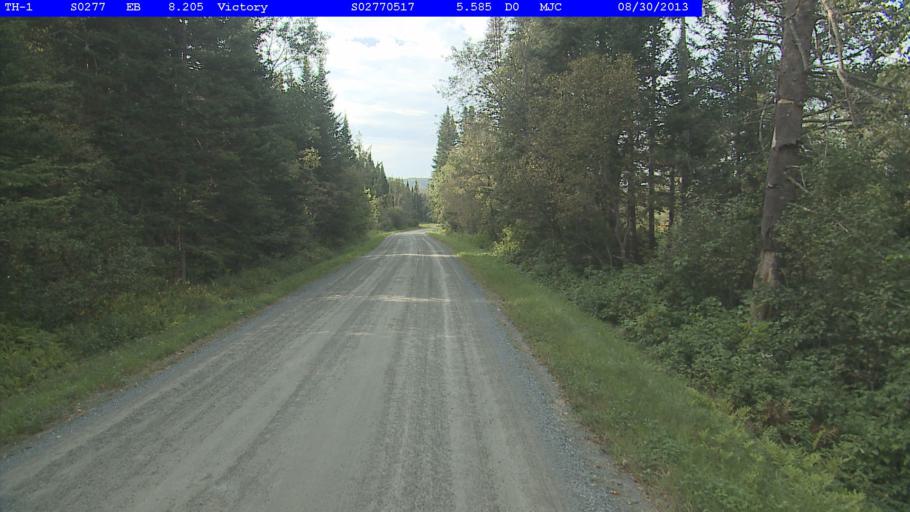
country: US
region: Vermont
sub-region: Caledonia County
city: Lyndonville
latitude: 44.5492
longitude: -71.7861
